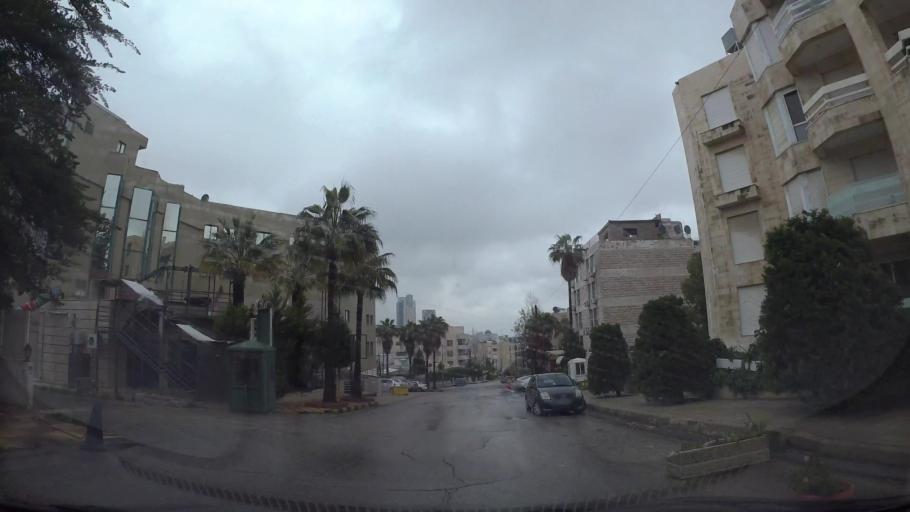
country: JO
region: Amman
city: Amman
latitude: 31.9576
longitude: 35.8995
